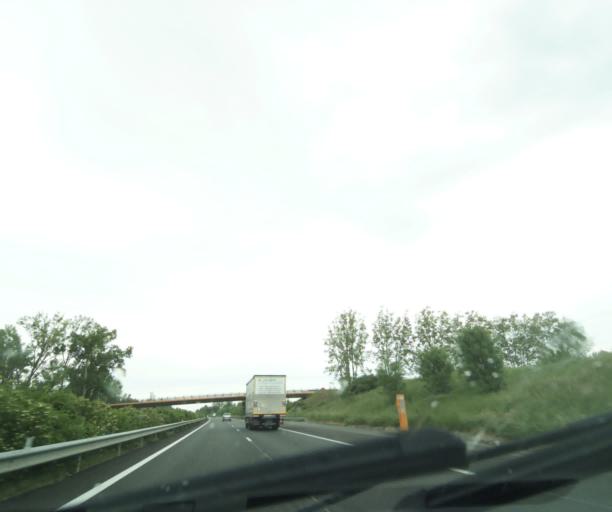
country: FR
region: Midi-Pyrenees
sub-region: Departement du Tarn-et-Garonne
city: Realville
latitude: 44.1169
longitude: 1.4729
